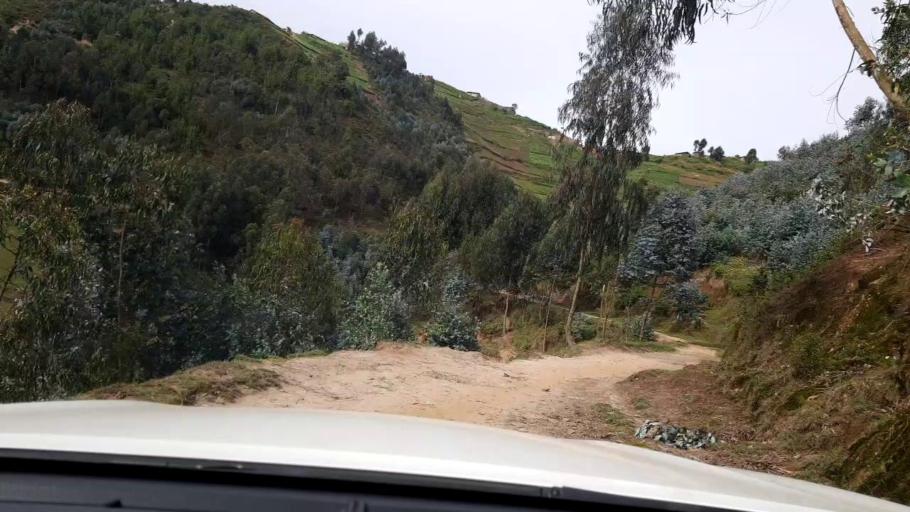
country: RW
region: Western Province
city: Kibuye
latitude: -1.8877
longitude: 29.4520
